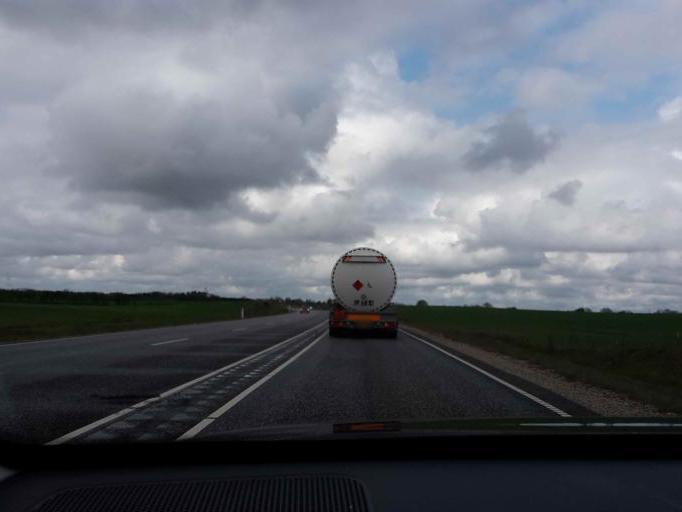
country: DK
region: South Denmark
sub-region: Vejle Kommune
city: Jelling
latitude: 55.6983
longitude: 9.3535
